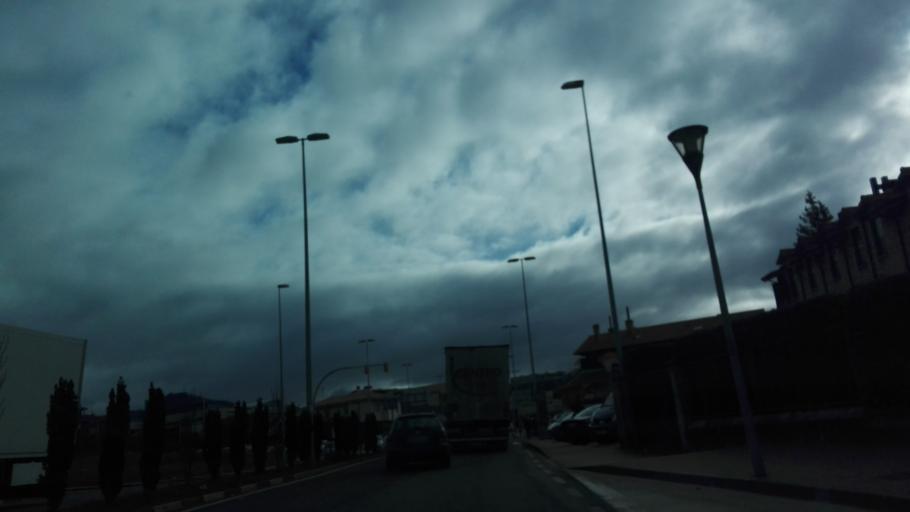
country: ES
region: Navarre
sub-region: Provincia de Navarra
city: Egues-Uharte
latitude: 42.8321
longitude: -1.5857
